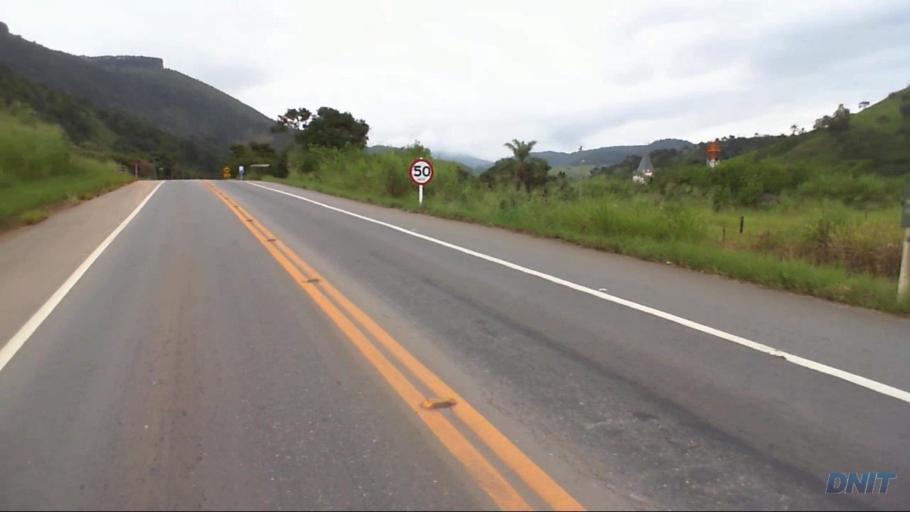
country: BR
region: Minas Gerais
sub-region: Nova Era
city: Nova Era
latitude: -19.7416
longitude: -43.0196
